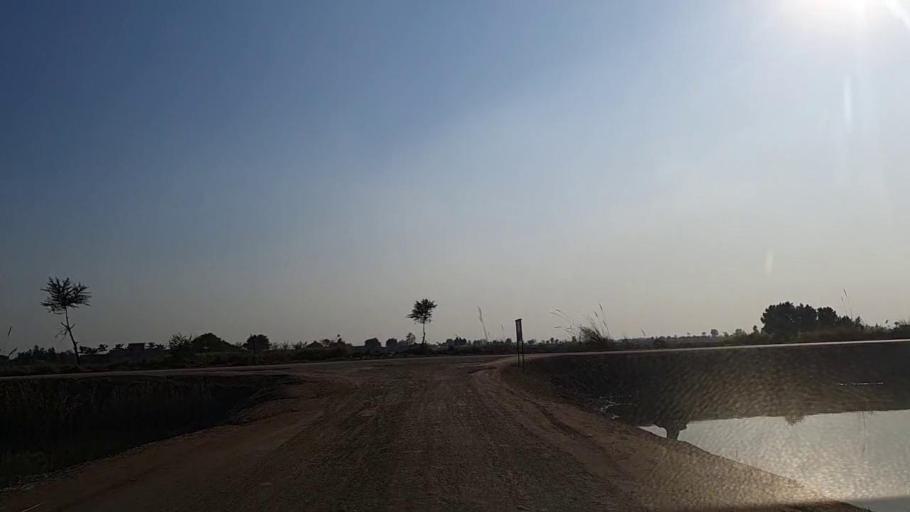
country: PK
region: Sindh
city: Daur
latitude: 26.4046
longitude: 68.2740
